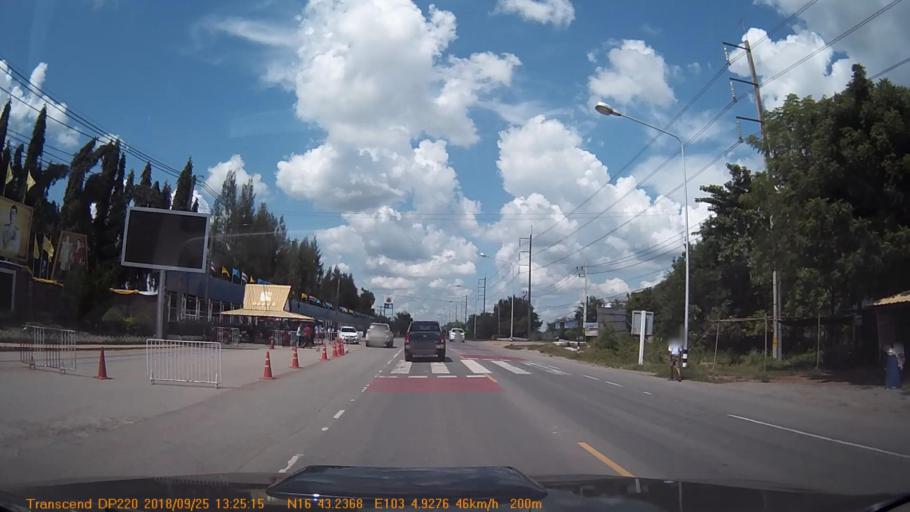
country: TH
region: Khon Kaen
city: Kranuan
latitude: 16.7205
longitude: 103.0821
